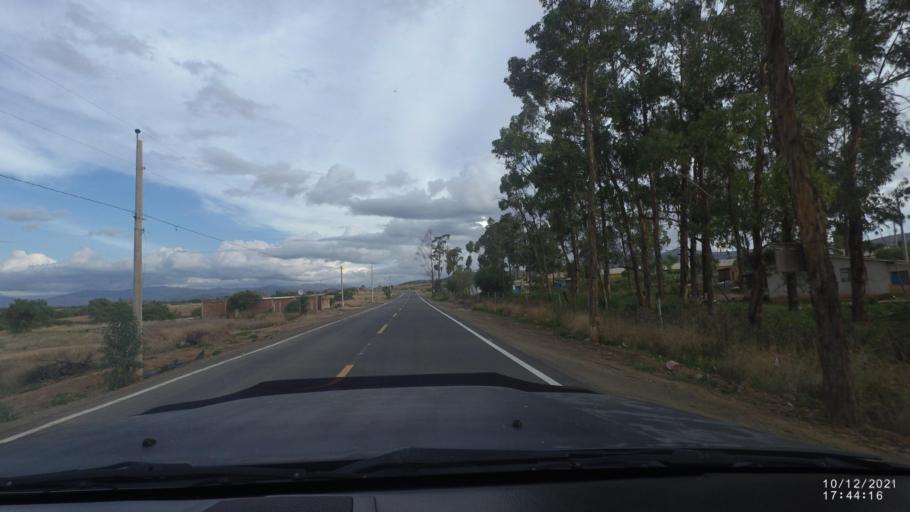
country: BO
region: Cochabamba
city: Tarata
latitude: -17.6187
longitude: -66.0145
